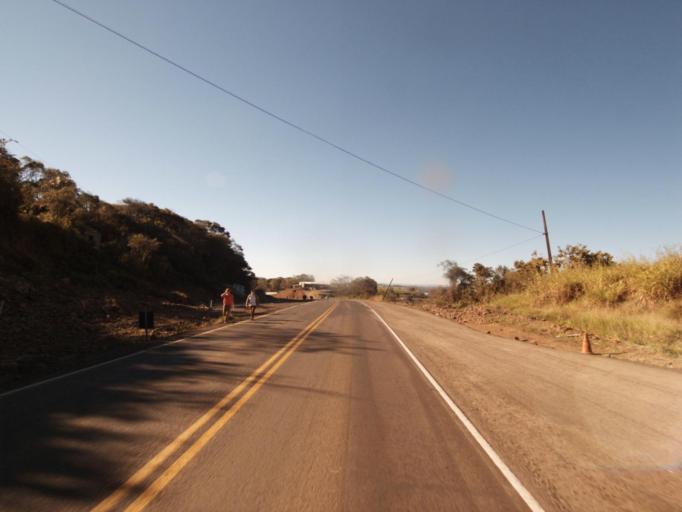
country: AR
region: Misiones
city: Bernardo de Irigoyen
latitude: -26.6922
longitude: -53.5151
